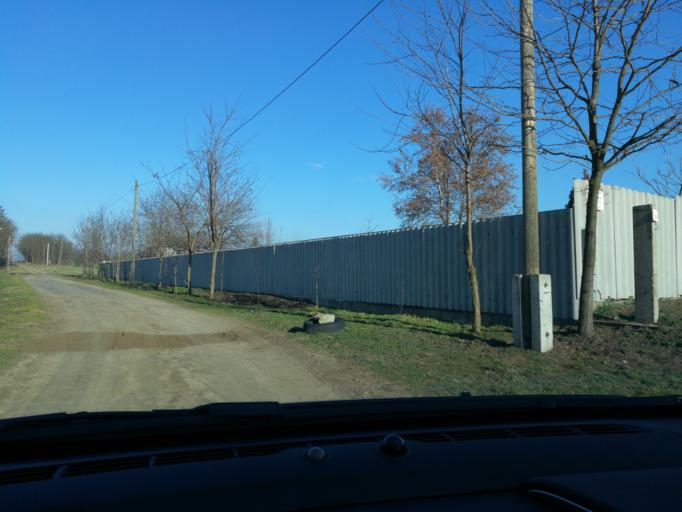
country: HU
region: Szabolcs-Szatmar-Bereg
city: Nyiregyhaza
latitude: 47.9693
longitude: 21.7572
